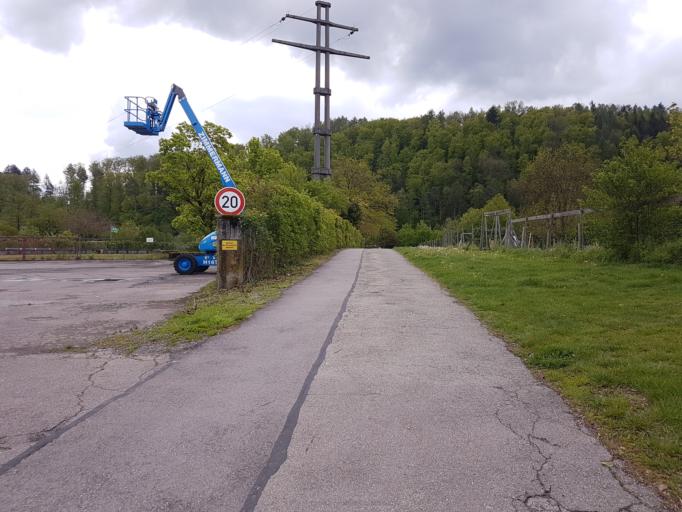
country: CH
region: Aargau
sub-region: Bezirk Zurzach
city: Koblenz
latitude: 47.6244
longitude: 8.2643
